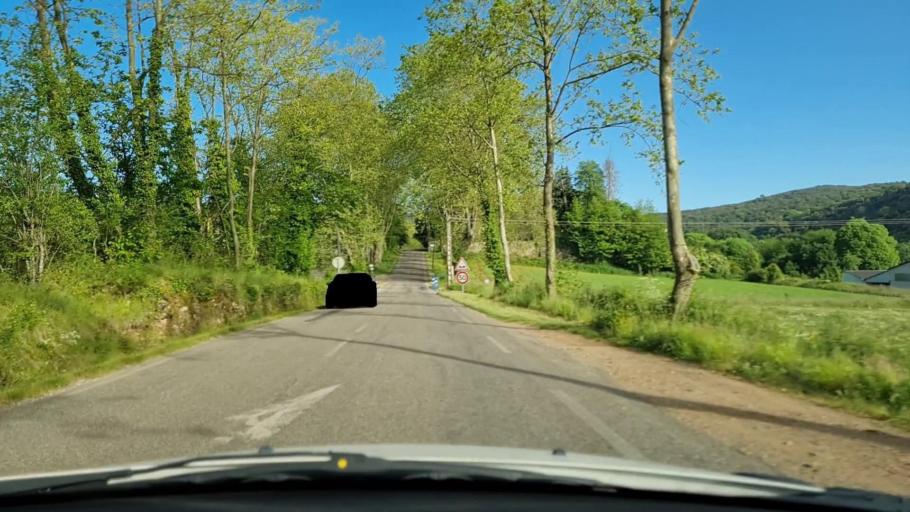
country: FR
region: Languedoc-Roussillon
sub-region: Departement du Gard
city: Cendras
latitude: 44.1501
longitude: 4.0475
